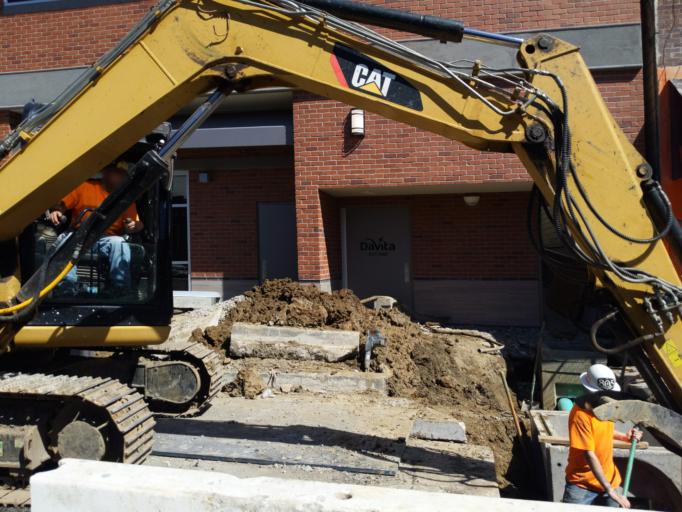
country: US
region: California
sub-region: Alameda County
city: Piedmont
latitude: 37.7915
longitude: -122.1985
